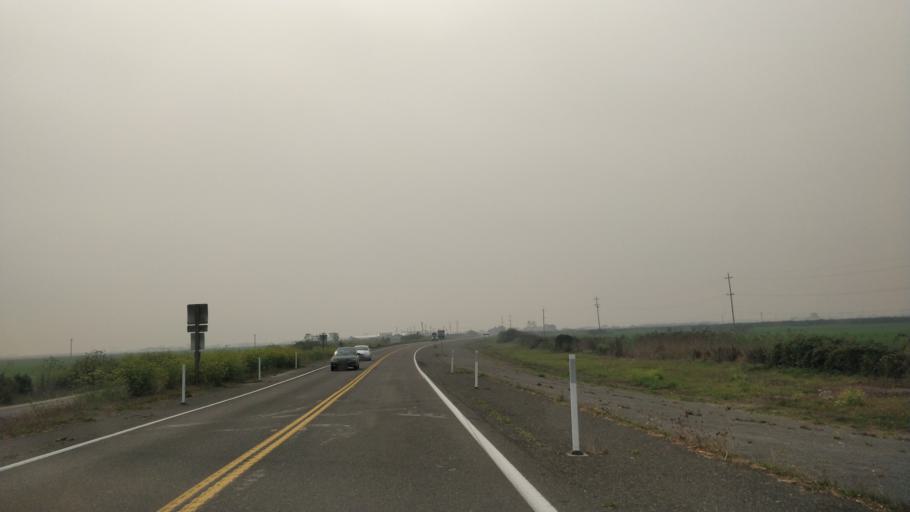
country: US
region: California
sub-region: Humboldt County
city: Fortuna
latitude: 40.6096
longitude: -124.2056
